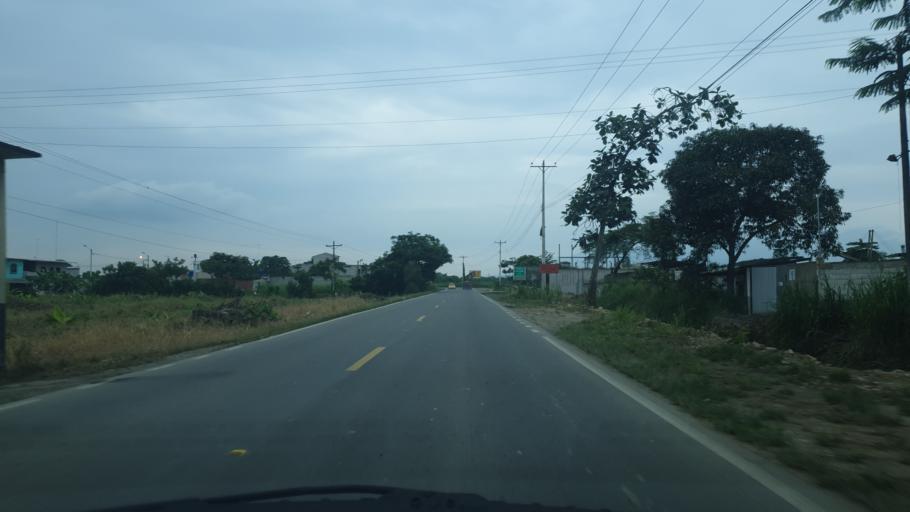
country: EC
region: El Oro
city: Pasaje
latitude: -3.3480
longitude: -79.8142
